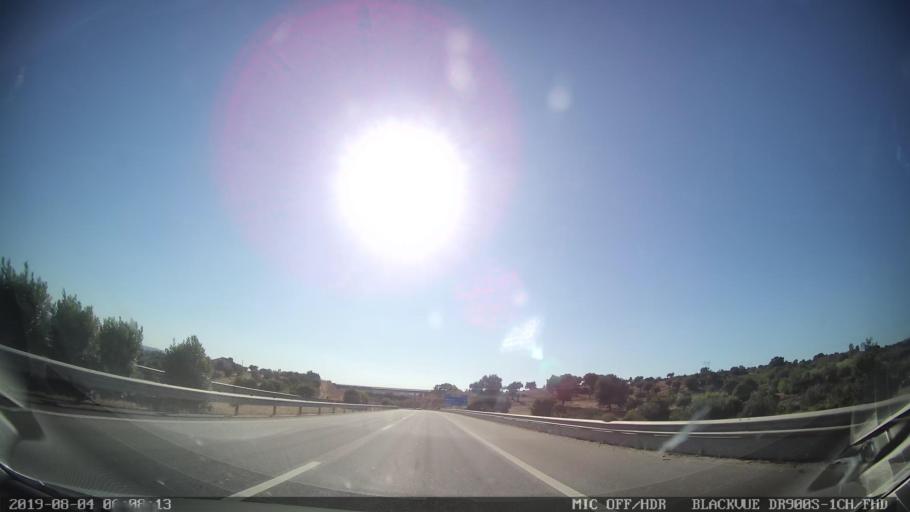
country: PT
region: Santarem
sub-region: Abrantes
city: Alferrarede
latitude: 39.4929
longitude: -8.1087
